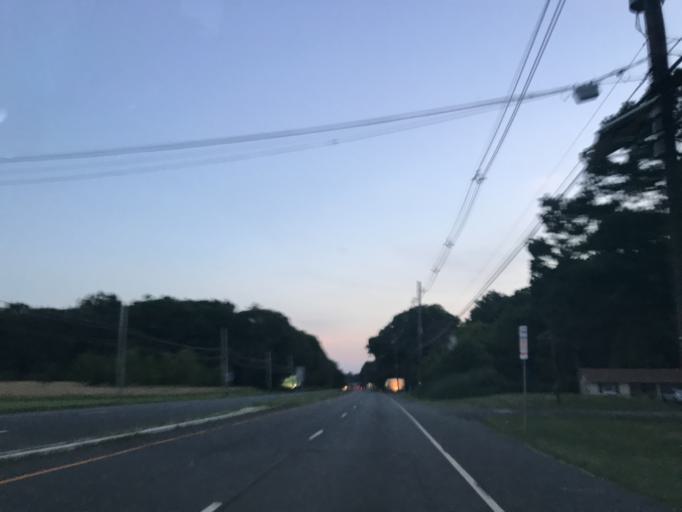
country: US
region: New Jersey
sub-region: Burlington County
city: Roebling
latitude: 40.1219
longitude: -74.7460
